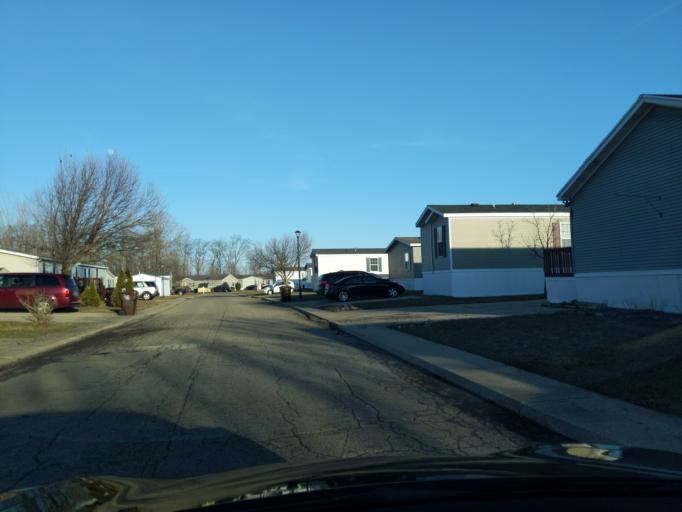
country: US
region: Michigan
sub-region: Jackson County
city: Jackson
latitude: 42.2827
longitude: -84.4769
